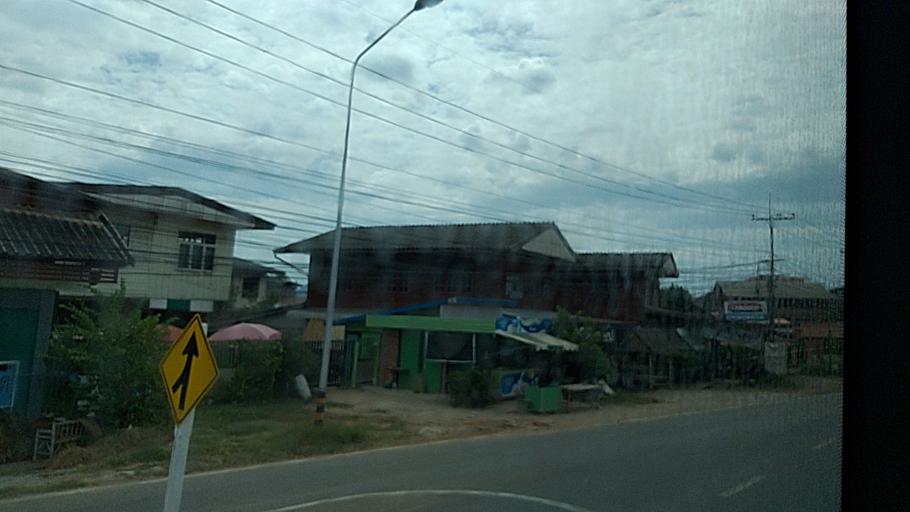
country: TH
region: Maha Sarakham
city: Kantharawichai
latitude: 16.2657
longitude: 103.2838
